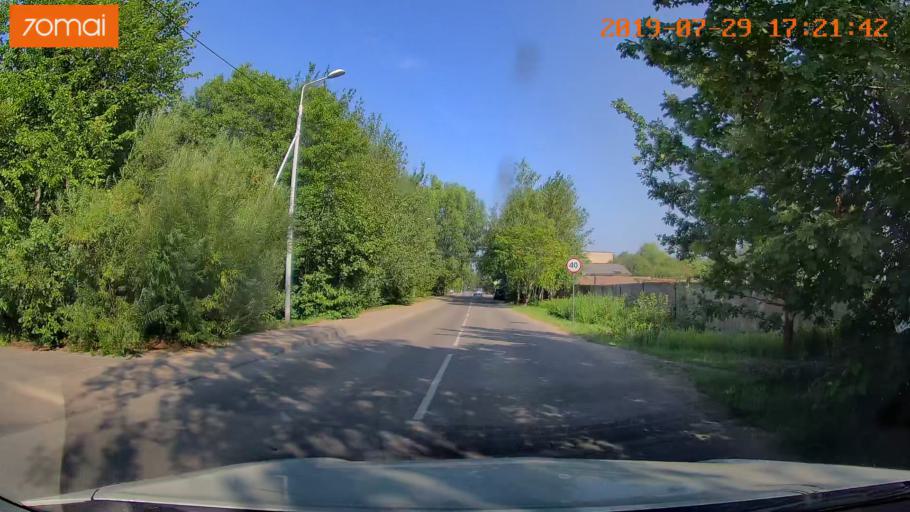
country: RU
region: Kaliningrad
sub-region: Gorod Kaliningrad
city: Kaliningrad
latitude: 54.7704
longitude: 20.4323
